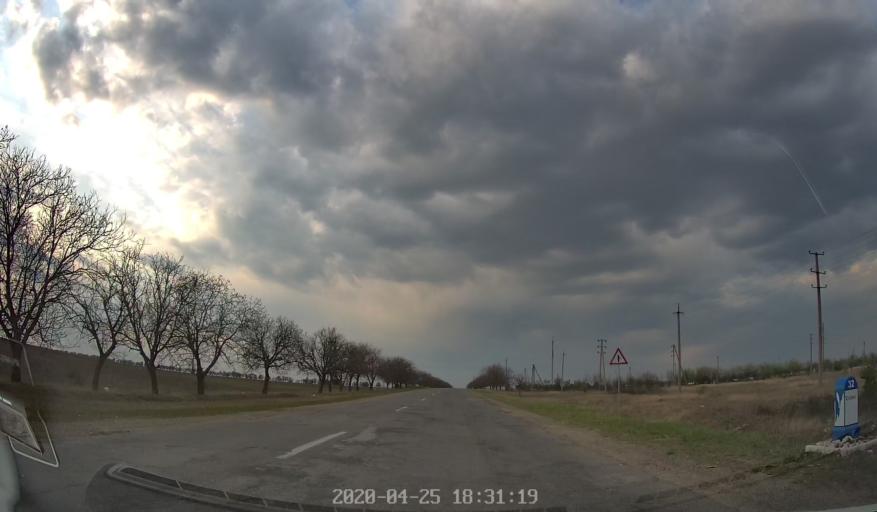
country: MD
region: Criuleni
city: Criuleni
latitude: 47.2160
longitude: 29.1477
